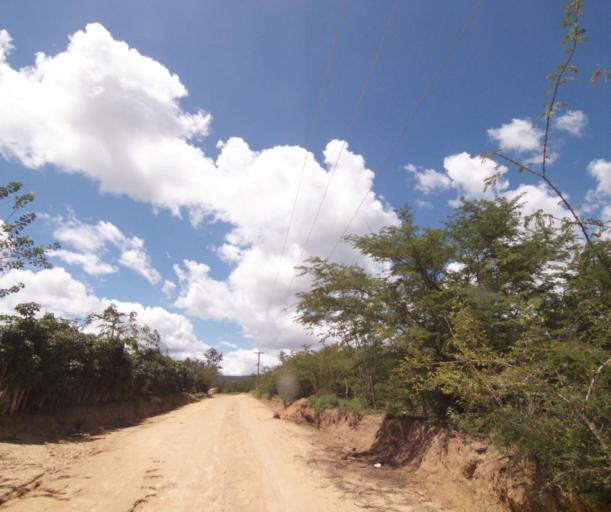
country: BR
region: Bahia
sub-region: Pocoes
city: Pocoes
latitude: -14.3738
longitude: -40.5677
